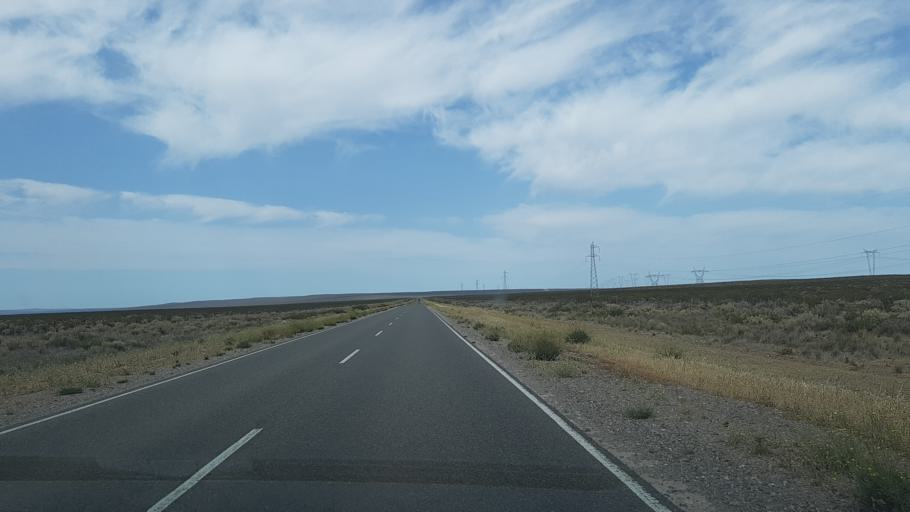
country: AR
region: Neuquen
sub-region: Departamento de Picun Leufu
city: Picun Leufu
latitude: -39.6936
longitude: -69.4827
